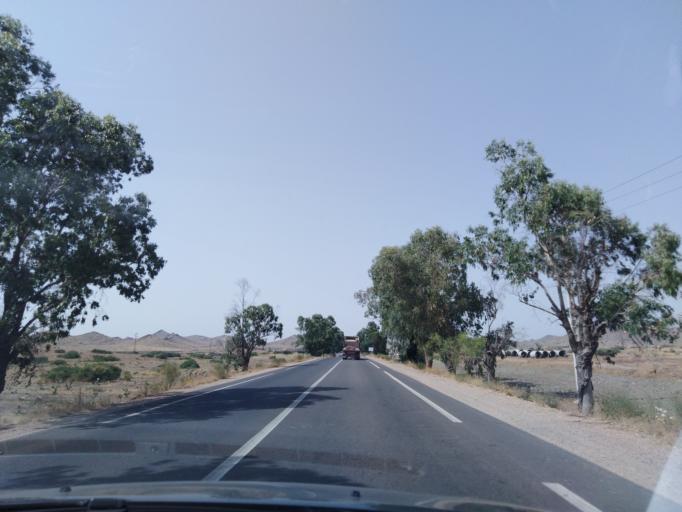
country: MA
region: Marrakech-Tensift-Al Haouz
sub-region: Kelaa-Des-Sraghna
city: Sidi Bou Othmane
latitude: 31.8238
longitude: -7.9735
